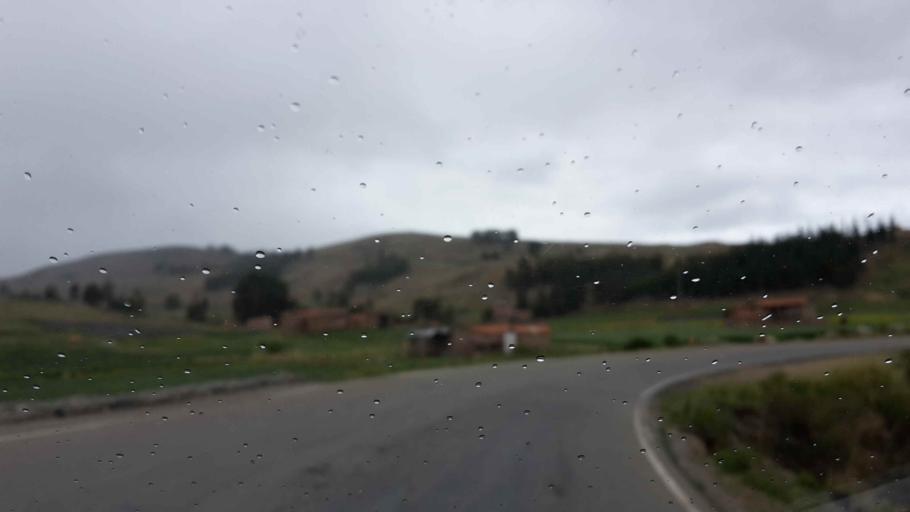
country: BO
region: Cochabamba
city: Arani
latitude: -17.4603
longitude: -65.6774
